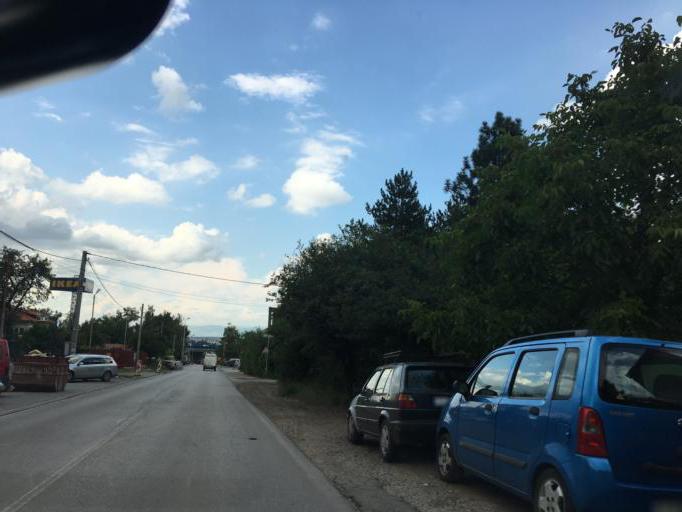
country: BG
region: Sofia-Capital
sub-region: Stolichna Obshtina
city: Sofia
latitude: 42.6211
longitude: 23.3587
